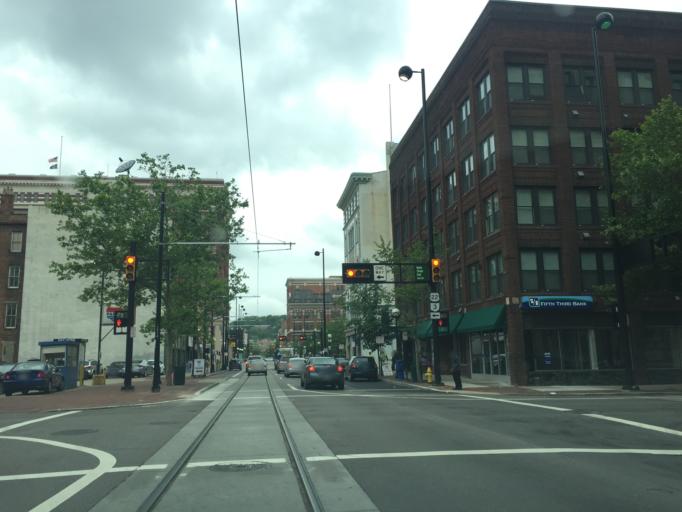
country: US
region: Kentucky
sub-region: Campbell County
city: Newport
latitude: 39.1057
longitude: -84.5108
